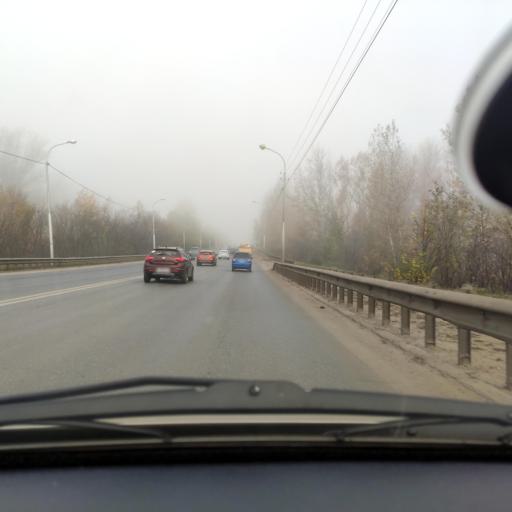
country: RU
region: Bashkortostan
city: Iglino
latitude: 54.7907
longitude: 56.2139
